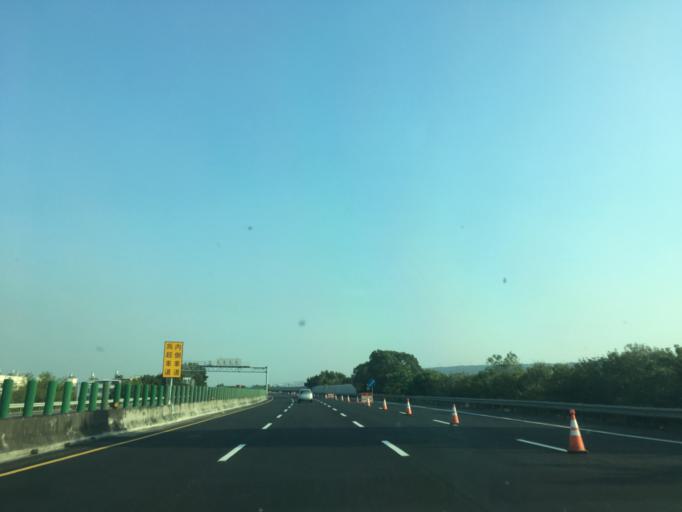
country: TW
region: Taiwan
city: Zhongxing New Village
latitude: 23.9984
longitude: 120.6501
